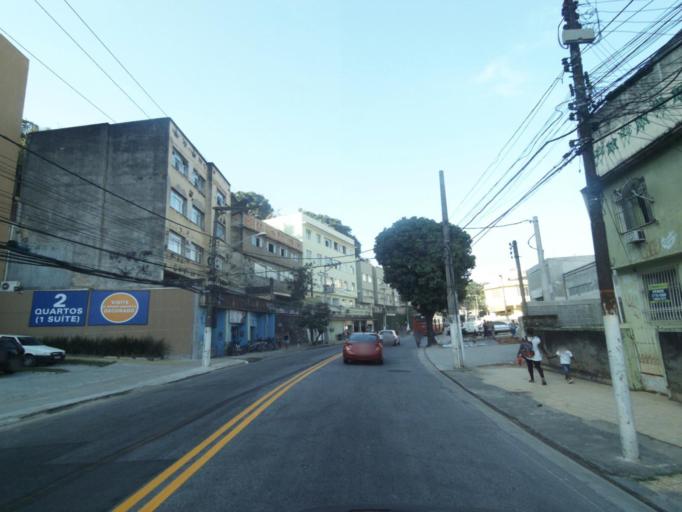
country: BR
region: Rio de Janeiro
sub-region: Niteroi
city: Niteroi
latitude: -22.8910
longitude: -43.0981
